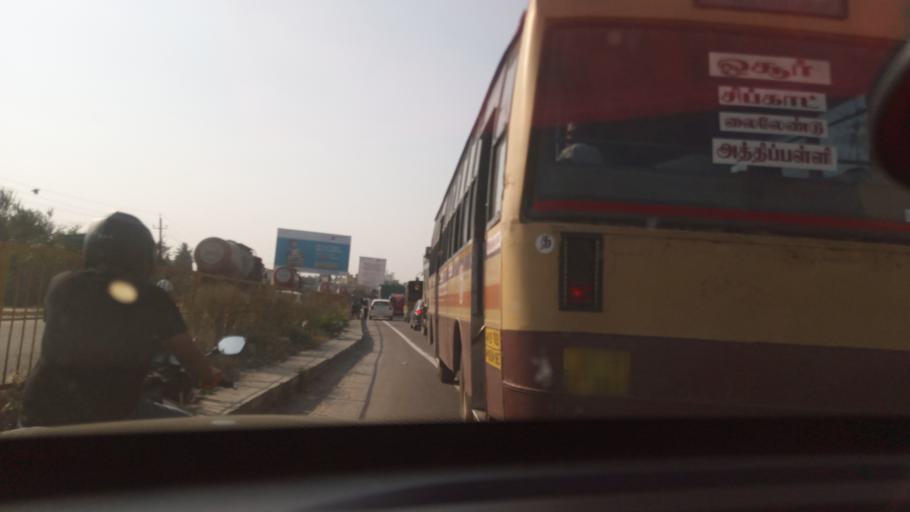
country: IN
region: Tamil Nadu
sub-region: Krishnagiri
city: Hosur
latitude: 12.7744
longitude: 77.7801
